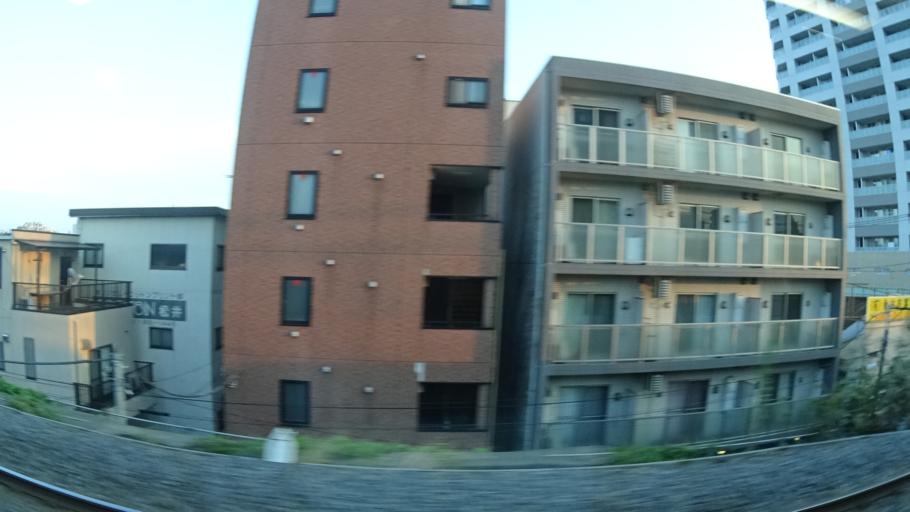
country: JP
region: Saitama
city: Soka
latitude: 35.7330
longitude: 139.7793
